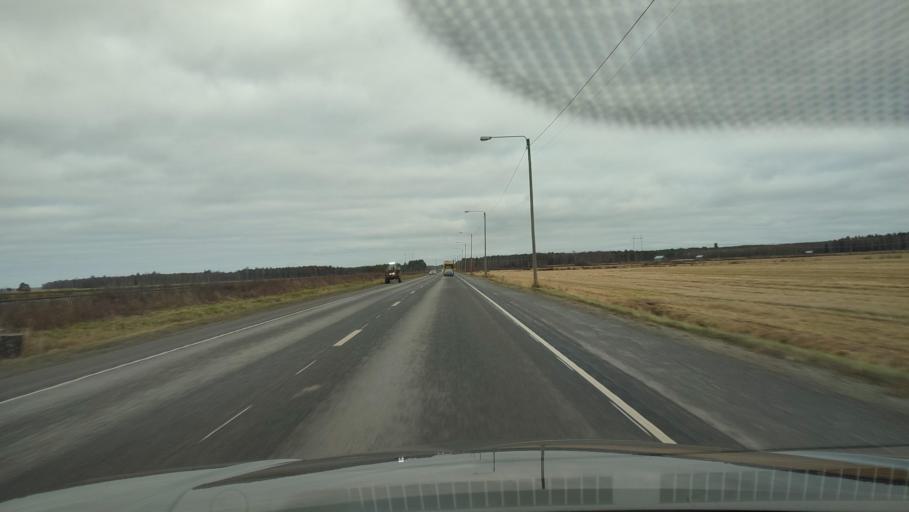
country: FI
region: Southern Ostrobothnia
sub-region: Seinaejoki
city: Ilmajoki
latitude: 62.7407
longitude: 22.6191
